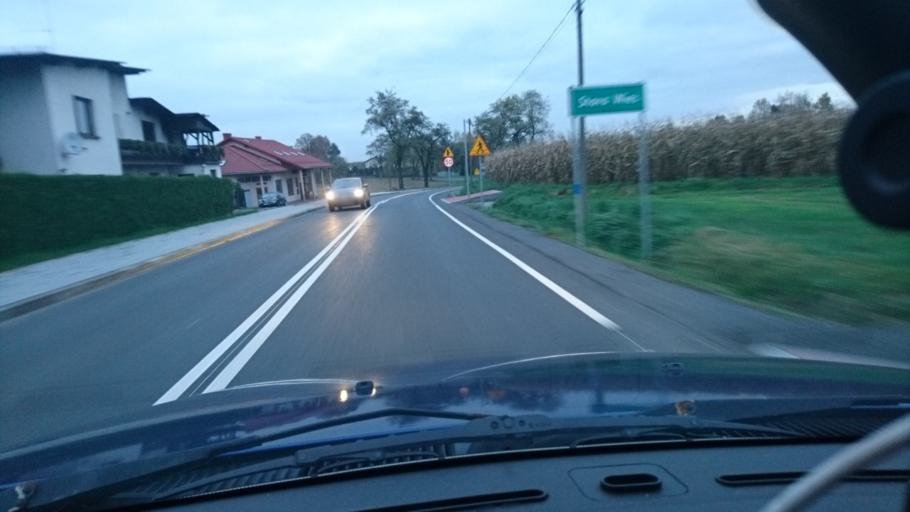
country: PL
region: Silesian Voivodeship
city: Janowice
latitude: 49.9085
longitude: 19.0928
